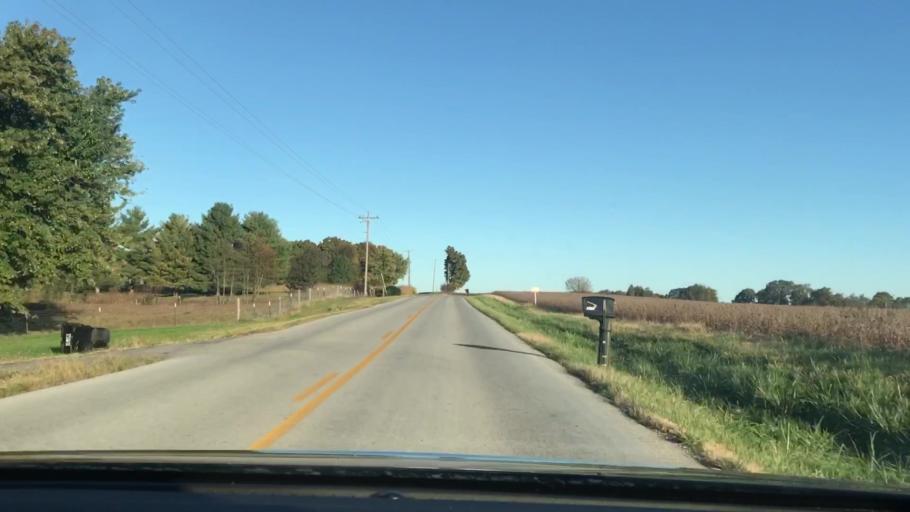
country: US
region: Kentucky
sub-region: Simpson County
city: Franklin
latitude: 36.7785
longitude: -86.6197
